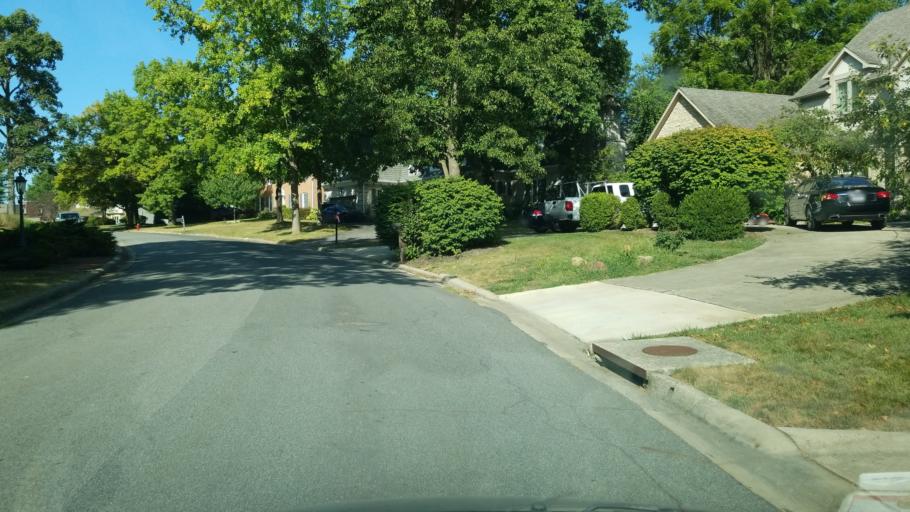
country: US
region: Ohio
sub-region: Delaware County
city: Powell
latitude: 40.1285
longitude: -83.0466
